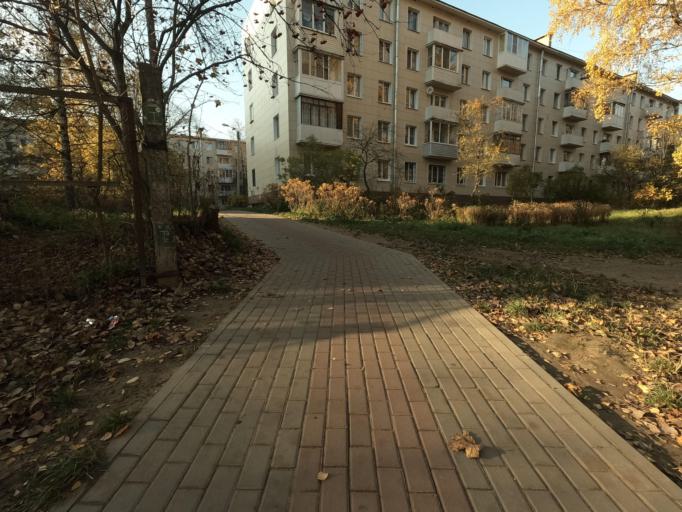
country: RU
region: Leningrad
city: Sertolovo
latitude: 60.1498
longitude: 30.2074
